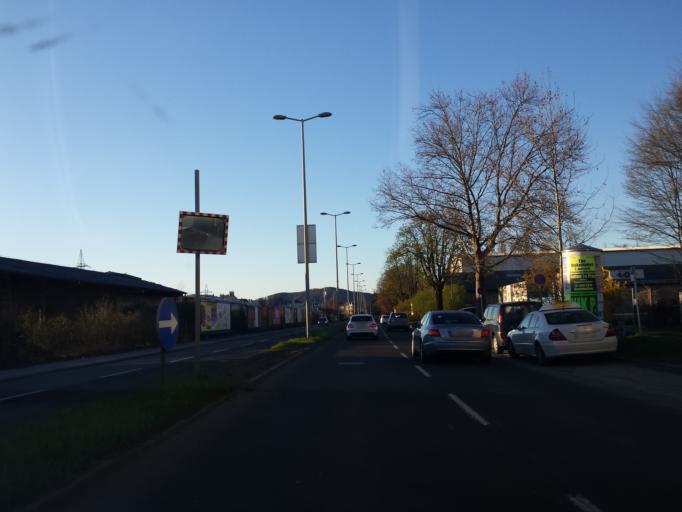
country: AT
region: Styria
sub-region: Graz Stadt
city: Goesting
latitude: 47.0772
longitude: 15.4169
